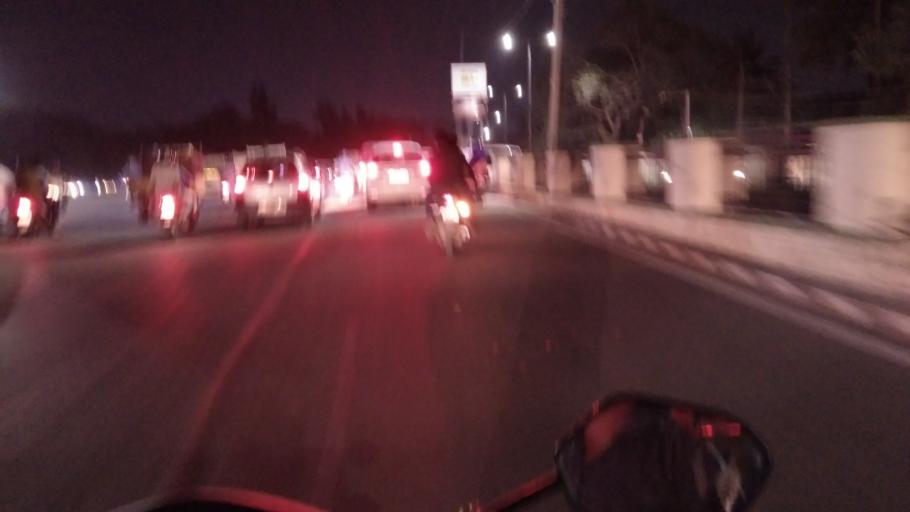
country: IN
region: Telangana
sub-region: Hyderabad
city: Malkajgiri
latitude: 17.4517
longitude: 78.4862
